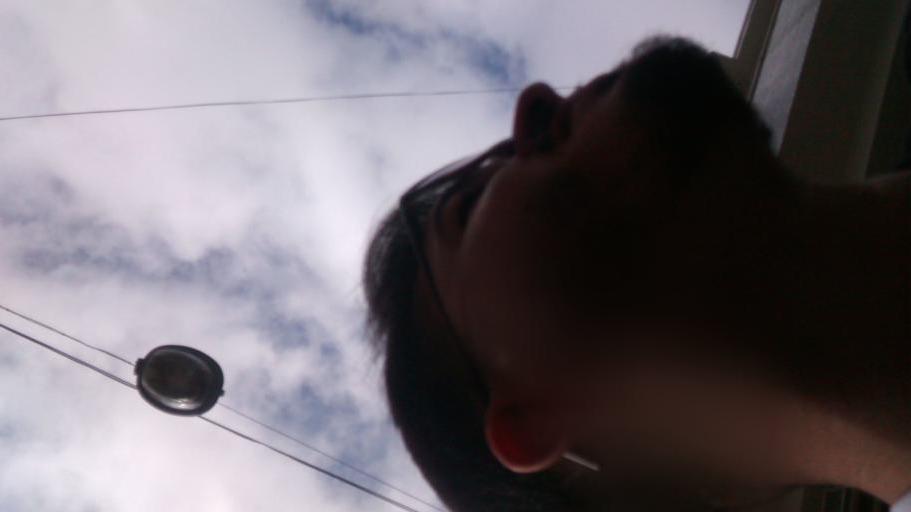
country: BR
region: Minas Gerais
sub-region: Itajuba
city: Itajuba
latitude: -22.4247
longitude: -45.4523
